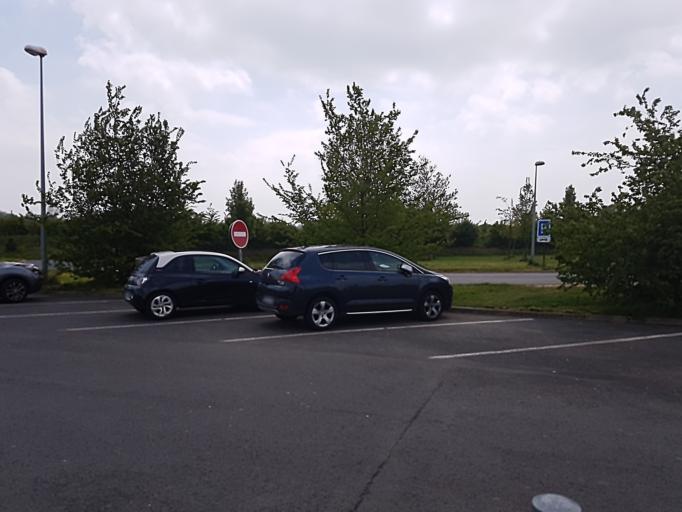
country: FR
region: Haute-Normandie
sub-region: Departement de l'Eure
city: Beuzeville
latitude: 49.3247
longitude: 0.3278
